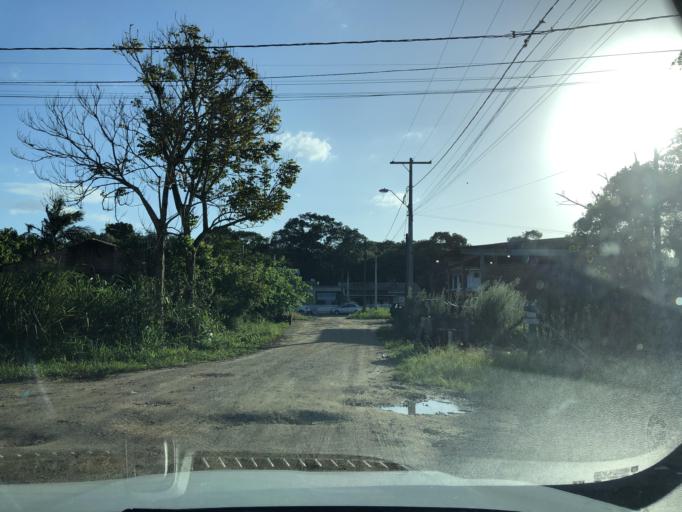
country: BR
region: Santa Catarina
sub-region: Sao Francisco Do Sul
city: Sao Francisco do Sul
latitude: -26.2152
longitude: -48.5327
